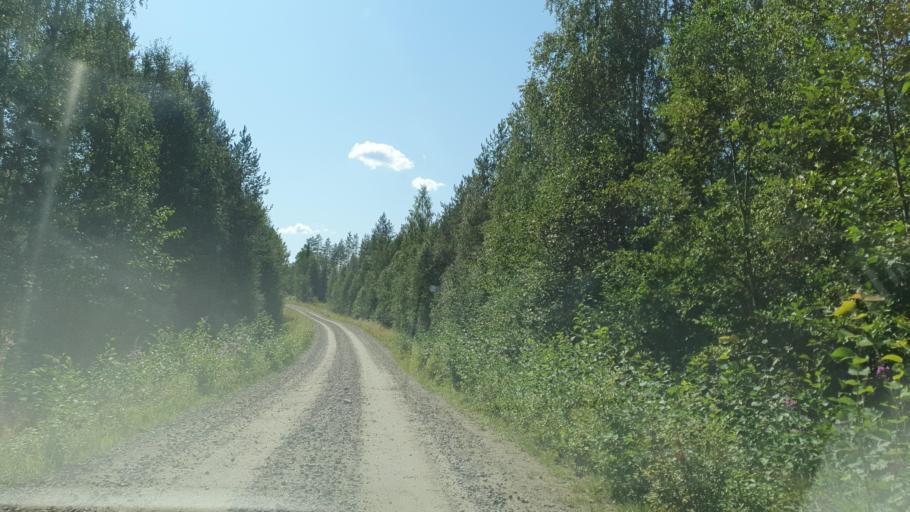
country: FI
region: Kainuu
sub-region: Kehys-Kainuu
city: Kuhmo
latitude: 64.0137
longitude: 29.5958
